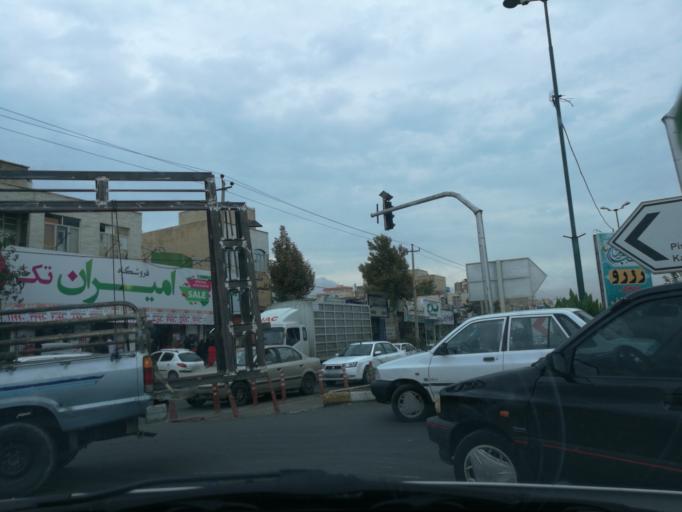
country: IR
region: Alborz
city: Karaj
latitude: 35.8452
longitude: 50.9200
